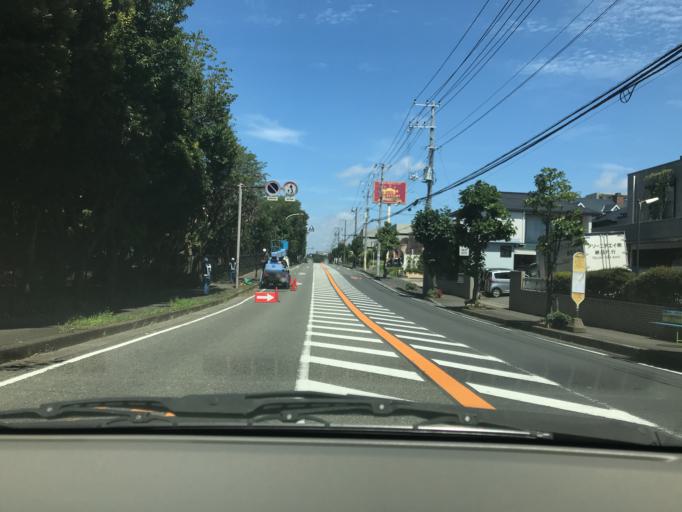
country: JP
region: Kanagawa
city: Fujisawa
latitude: 35.3558
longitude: 139.4675
